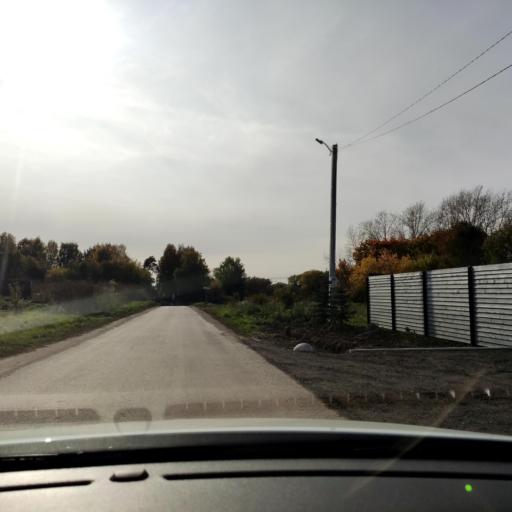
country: RU
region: Tatarstan
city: Vysokaya Gora
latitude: 55.8725
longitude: 49.3744
